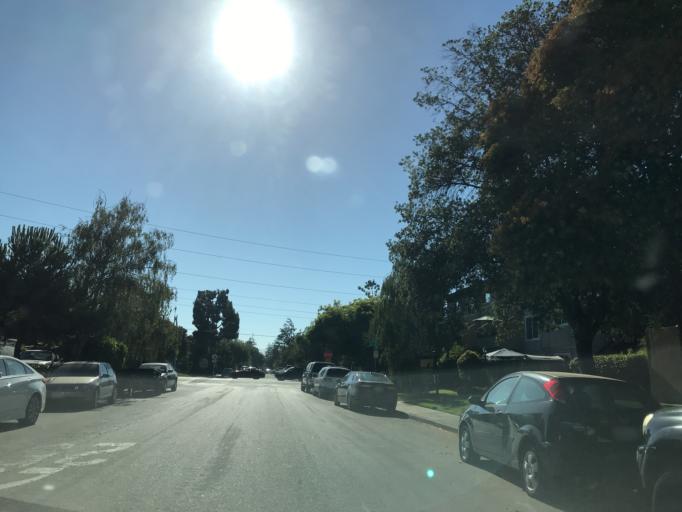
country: US
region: California
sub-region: Santa Clara County
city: Mountain View
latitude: 37.4125
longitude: -122.0915
